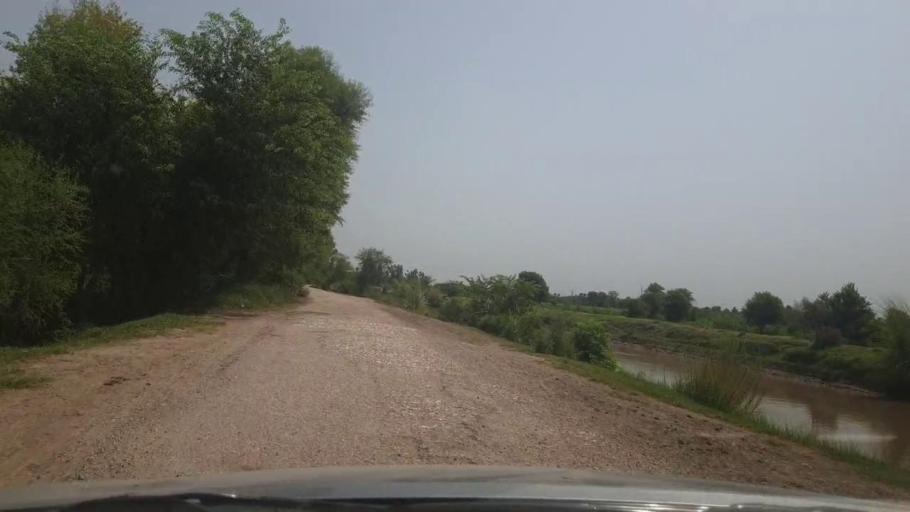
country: PK
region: Sindh
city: Pano Aqil
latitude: 27.8969
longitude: 69.1426
